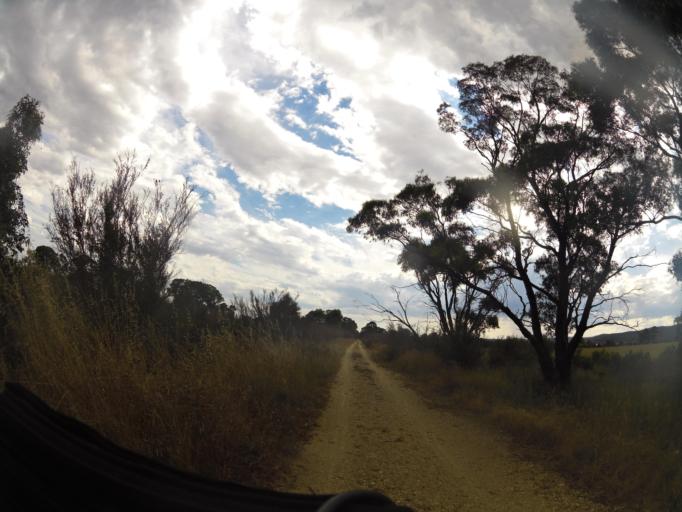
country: AU
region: Victoria
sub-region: Wellington
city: Heyfield
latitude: -38.0414
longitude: 146.6453
